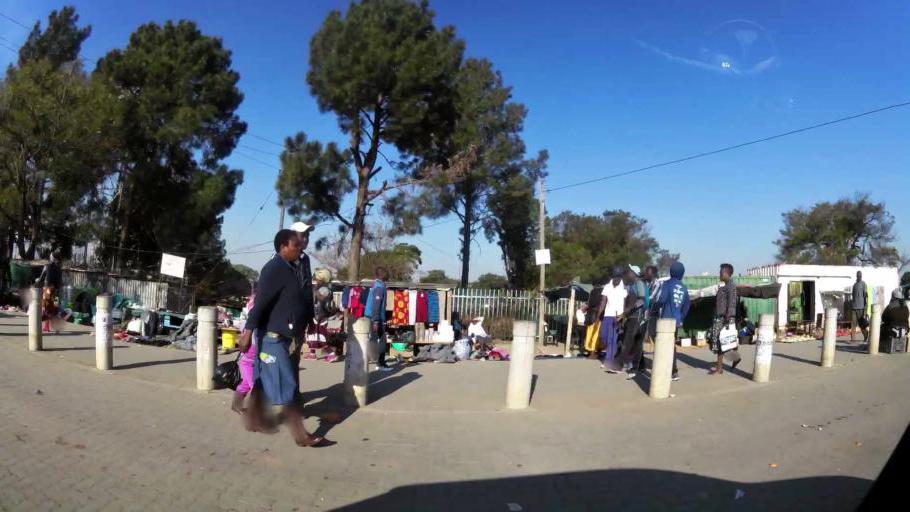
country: ZA
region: Gauteng
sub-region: West Rand District Municipality
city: Muldersdriseloop
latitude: -26.0580
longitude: 27.9029
